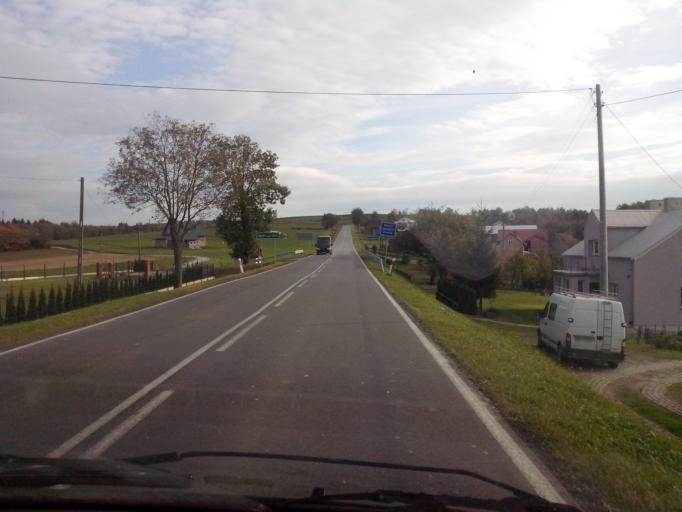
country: PL
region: Subcarpathian Voivodeship
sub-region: Powiat ropczycko-sedziszowski
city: Wielopole Skrzynskie
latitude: 49.9218
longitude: 21.6113
